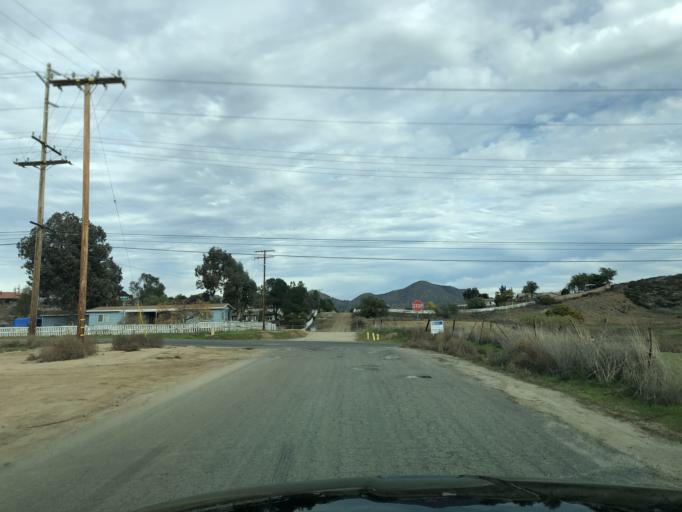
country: US
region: California
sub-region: Riverside County
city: Wildomar
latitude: 33.6100
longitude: -117.2839
